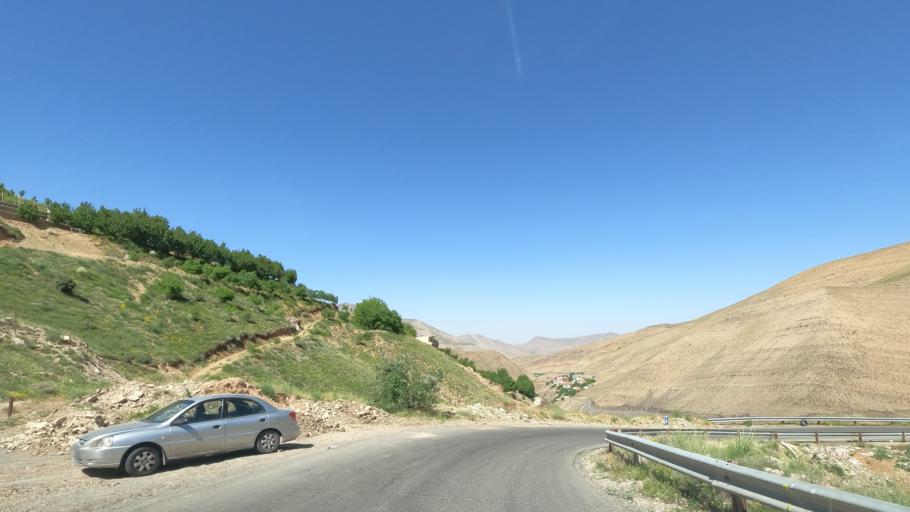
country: IR
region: Alborz
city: Karaj
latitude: 35.9224
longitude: 51.1574
